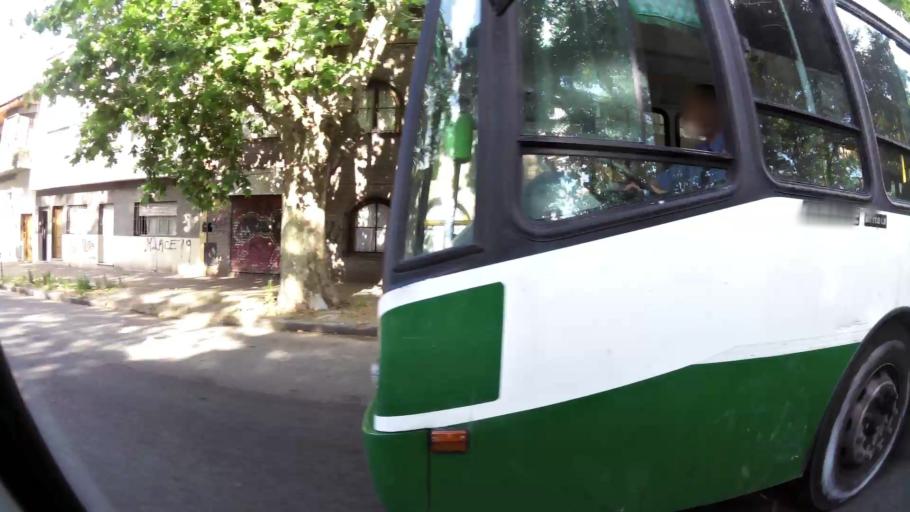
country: AR
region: Buenos Aires
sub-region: Partido de La Plata
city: La Plata
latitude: -34.8988
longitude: -57.9494
